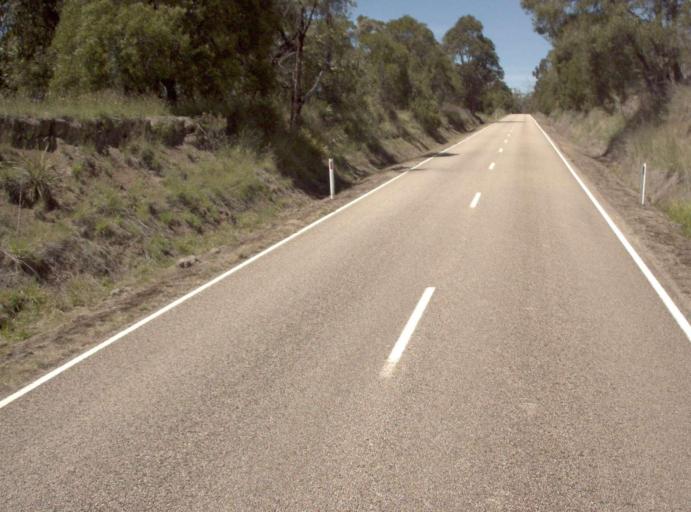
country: AU
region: Victoria
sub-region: East Gippsland
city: Lakes Entrance
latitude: -37.2533
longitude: 148.2488
